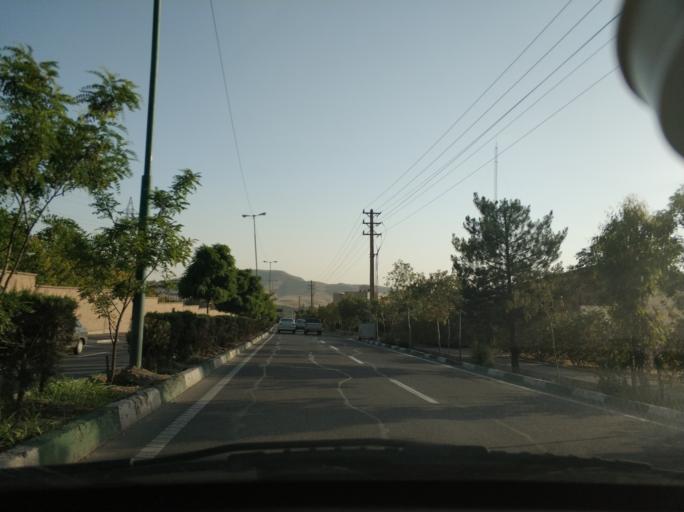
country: IR
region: Tehran
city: Tehran
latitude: 35.7301
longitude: 51.5933
